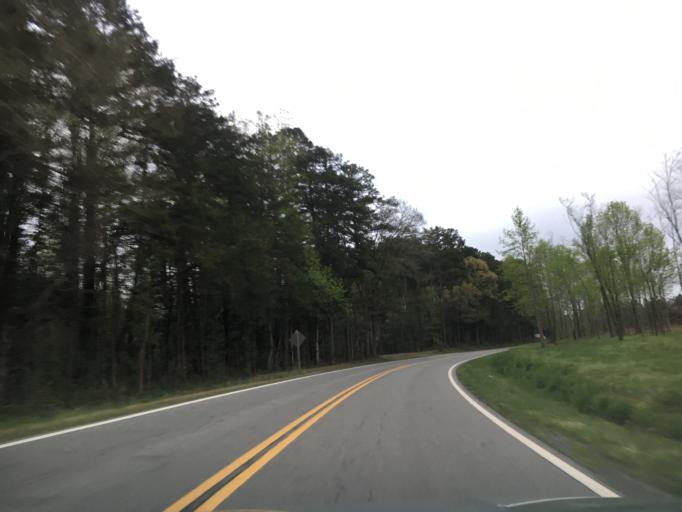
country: US
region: Virginia
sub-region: Halifax County
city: South Boston
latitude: 36.6810
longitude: -78.8955
